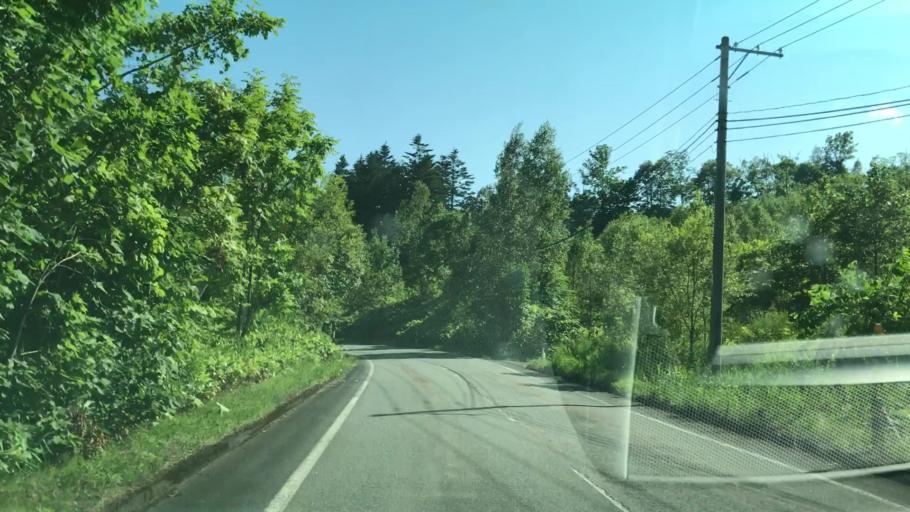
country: JP
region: Hokkaido
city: Shimo-furano
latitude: 42.8615
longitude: 142.4404
